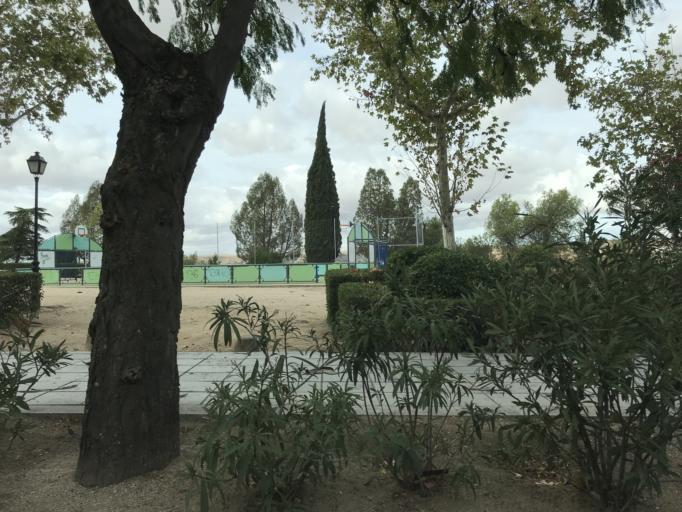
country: ES
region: Castille-La Mancha
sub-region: Province of Toledo
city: Toledo
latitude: 39.8610
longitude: -4.0300
